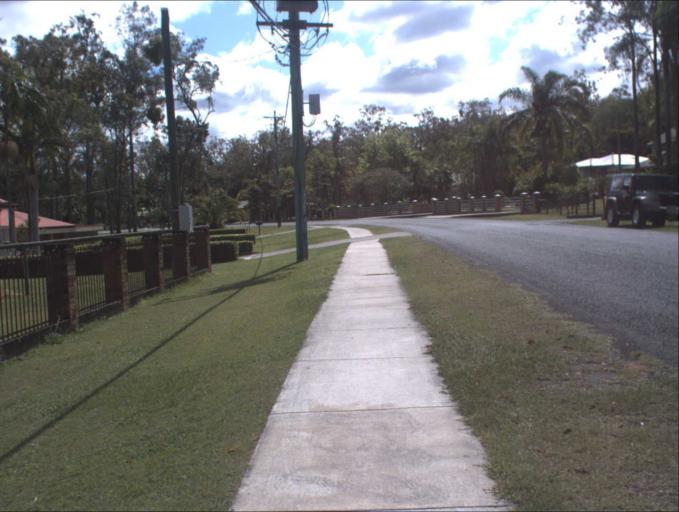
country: AU
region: Queensland
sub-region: Logan
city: Park Ridge South
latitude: -27.7456
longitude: 153.0223
